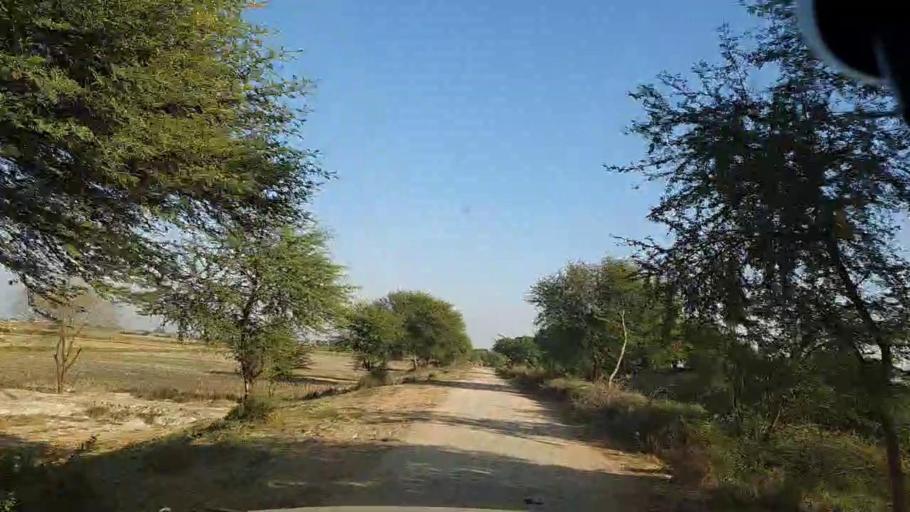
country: PK
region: Sindh
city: Chuhar Jamali
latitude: 24.5617
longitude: 68.0694
